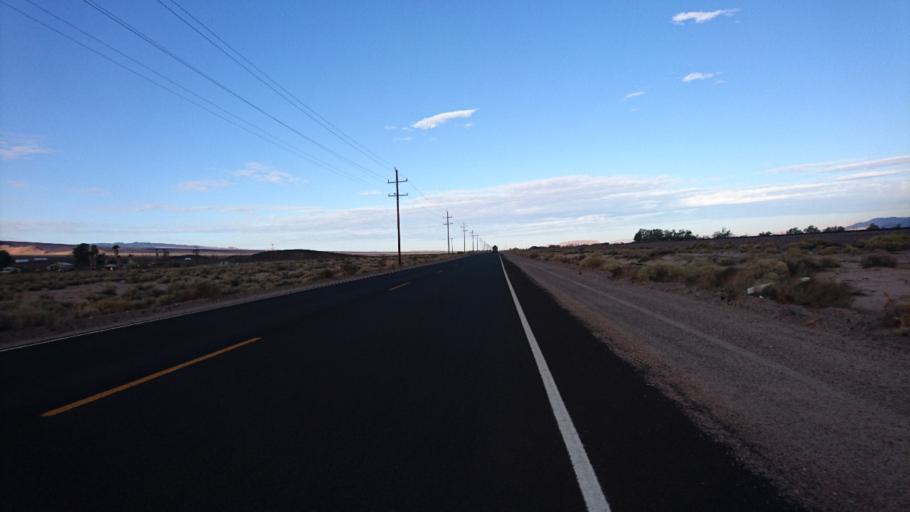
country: US
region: California
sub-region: San Bernardino County
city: Barstow
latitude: 34.8372
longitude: -116.7208
